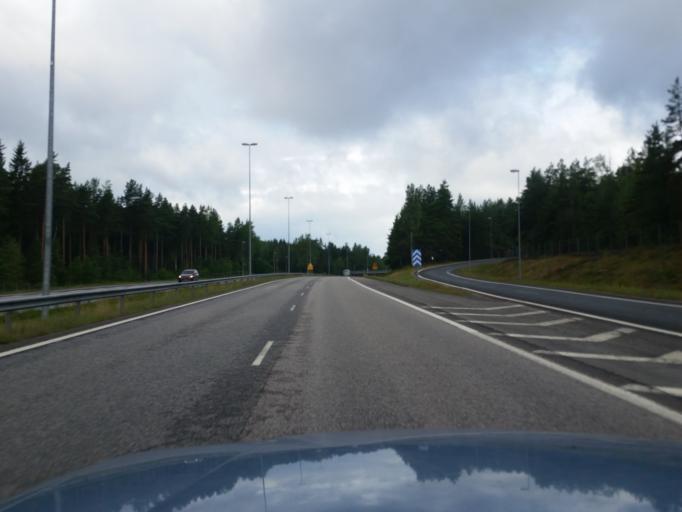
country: FI
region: Uusimaa
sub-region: Helsinki
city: Kirkkonummi
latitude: 60.2716
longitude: 24.4601
